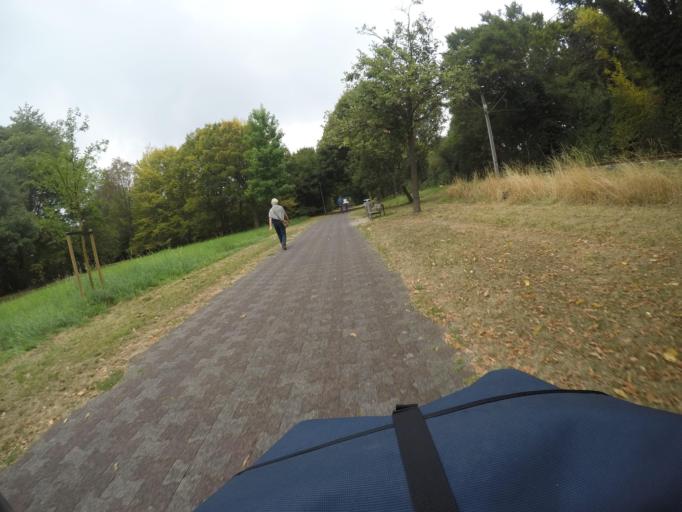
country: DE
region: North Rhine-Westphalia
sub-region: Regierungsbezirk Dusseldorf
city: Krefeld
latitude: 51.3108
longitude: 6.5931
